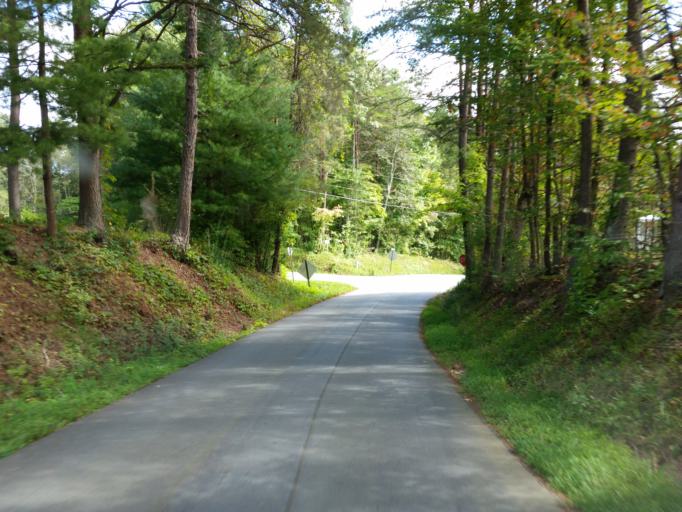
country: US
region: Georgia
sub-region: Fannin County
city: Blue Ridge
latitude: 34.8692
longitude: -84.2375
